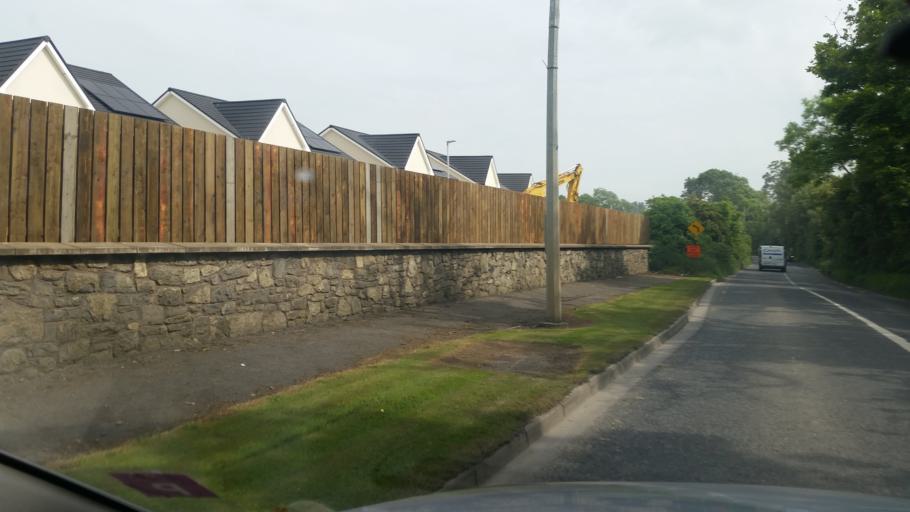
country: IE
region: Leinster
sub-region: Fingal County
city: Swords
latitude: 53.4544
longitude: -6.2647
